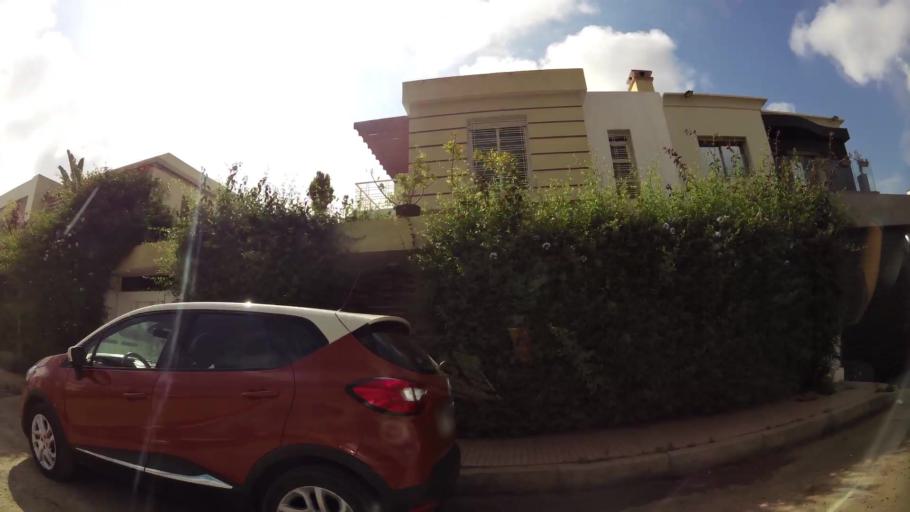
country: MA
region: Rabat-Sale-Zemmour-Zaer
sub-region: Skhirate-Temara
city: Temara
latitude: 33.9479
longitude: -6.8776
